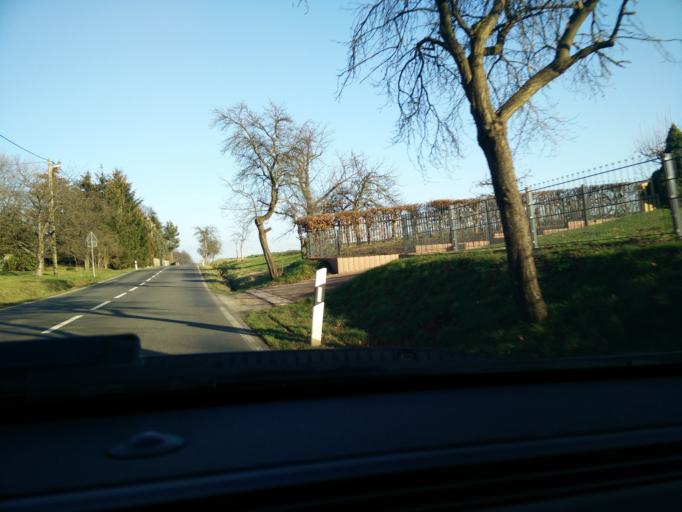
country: DE
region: Saxony
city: Geithain
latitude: 51.0669
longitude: 12.7125
